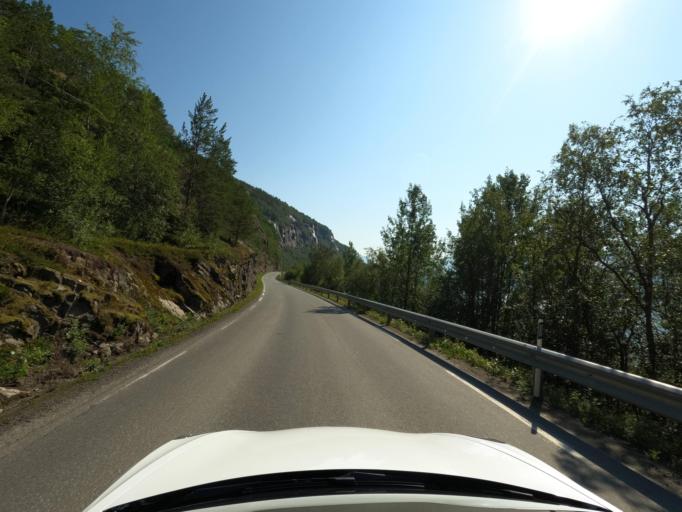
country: NO
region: Nordland
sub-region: Narvik
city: Narvik
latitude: 68.3548
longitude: 17.2730
